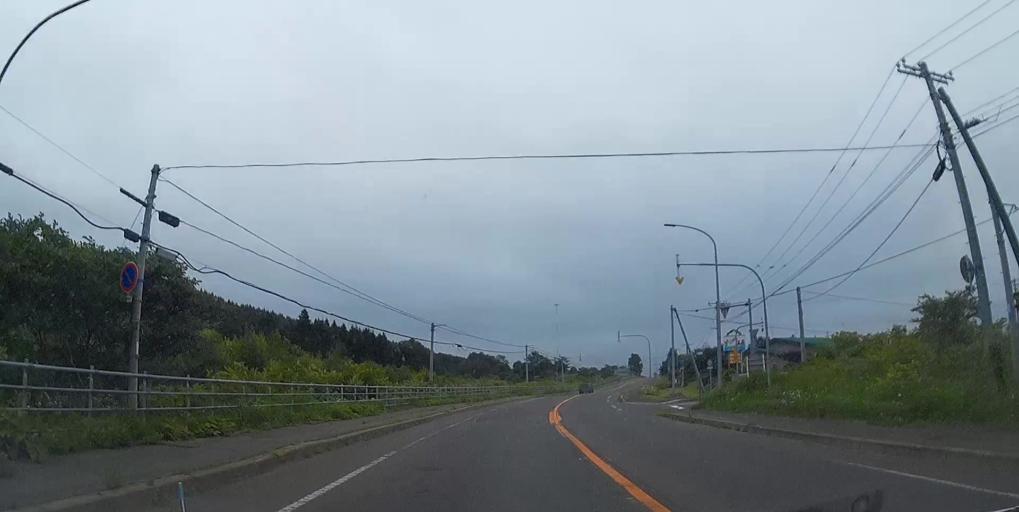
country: JP
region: Hokkaido
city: Iwanai
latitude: 42.4325
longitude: 139.9375
